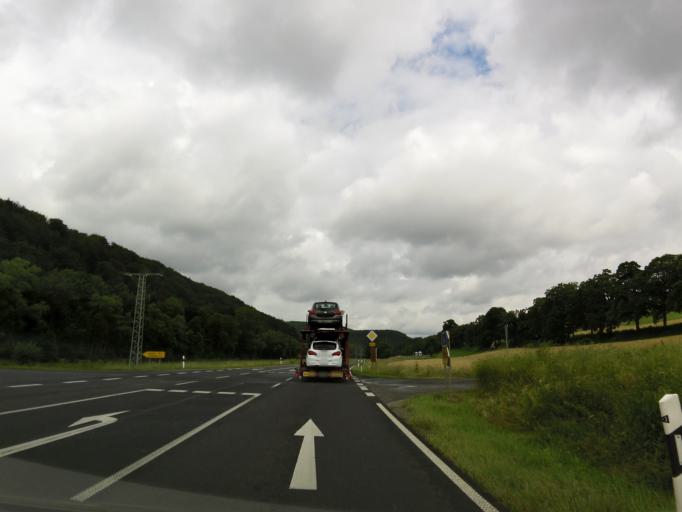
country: DE
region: Hesse
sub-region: Regierungsbezirk Kassel
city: Sontra
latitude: 51.0517
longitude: 10.0078
